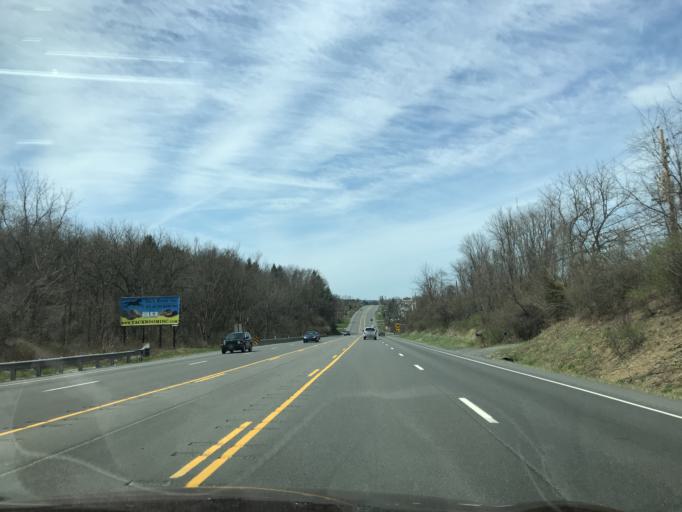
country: US
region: Pennsylvania
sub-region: Union County
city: Lewisburg
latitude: 40.9384
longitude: -76.8759
